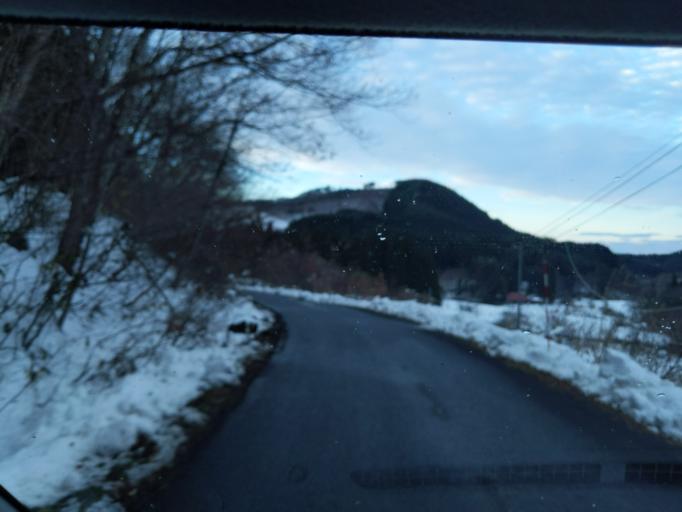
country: JP
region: Iwate
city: Mizusawa
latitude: 39.0436
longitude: 141.0203
